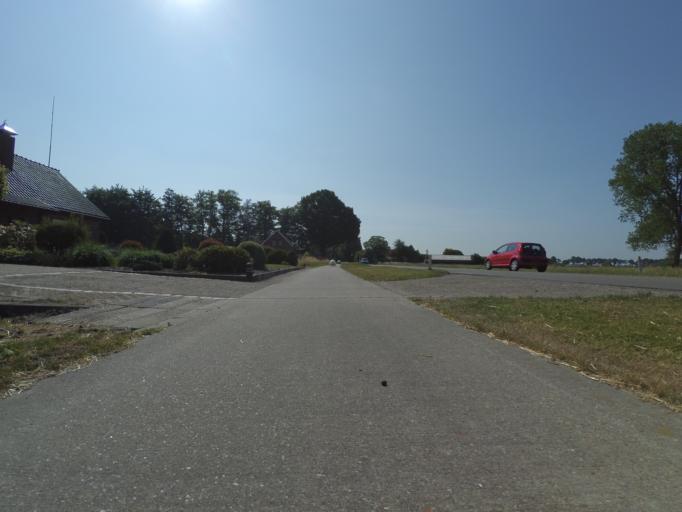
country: NL
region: North Brabant
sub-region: Gemeente Zundert
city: Zundert
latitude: 51.4799
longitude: 4.6183
